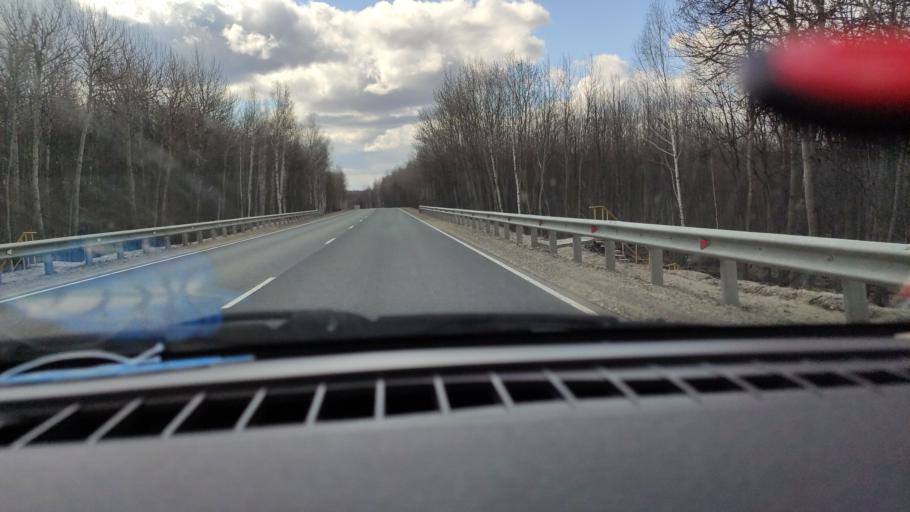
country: RU
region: Saratov
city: Khvalynsk
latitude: 52.4440
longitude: 48.0098
